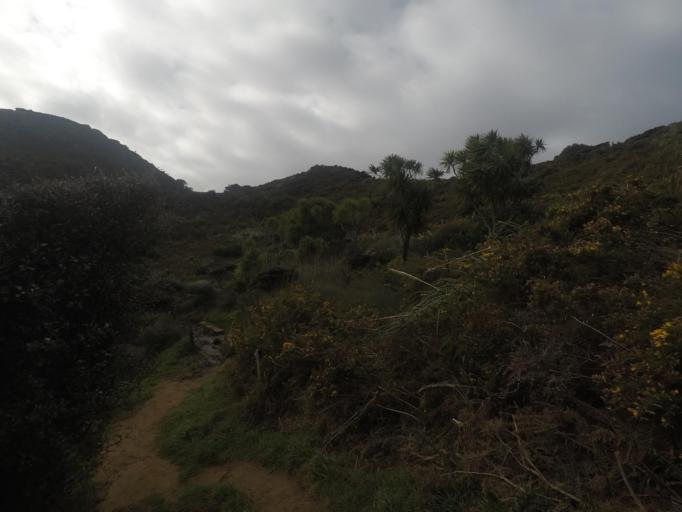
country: NZ
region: Auckland
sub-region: Auckland
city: Muriwai Beach
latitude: -36.8785
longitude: 174.4315
